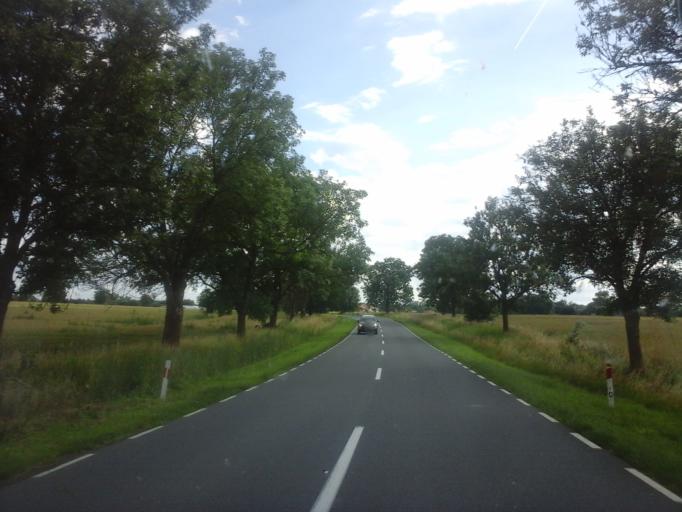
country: PL
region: West Pomeranian Voivodeship
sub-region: Powiat stargardzki
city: Suchan
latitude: 53.2355
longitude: 15.3026
